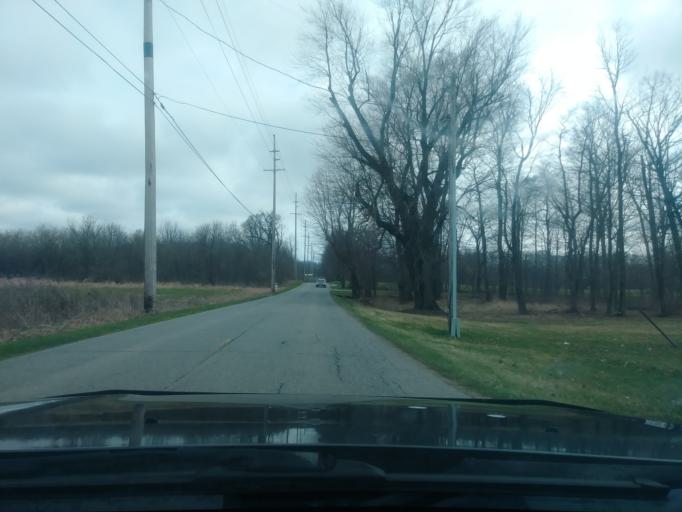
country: US
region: Indiana
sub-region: LaPorte County
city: LaPorte
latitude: 41.6342
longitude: -86.7970
